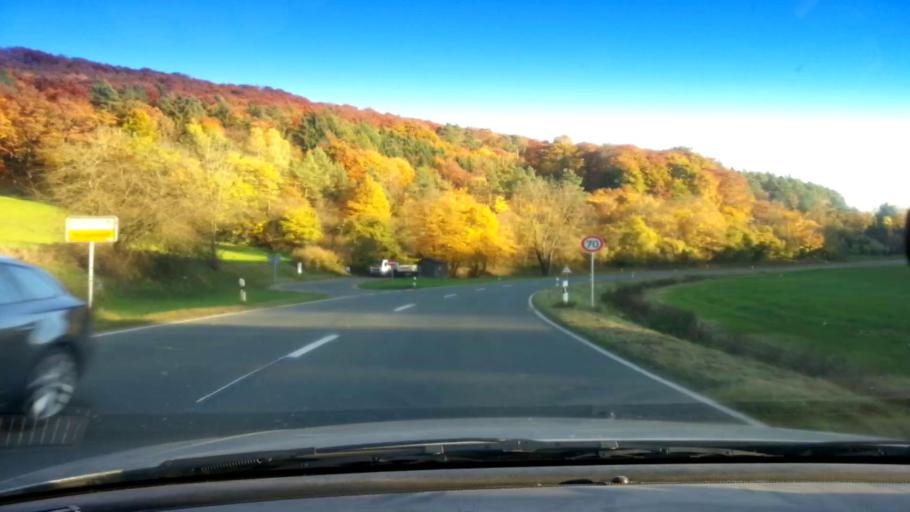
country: DE
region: Bavaria
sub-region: Upper Franconia
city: Heiligenstadt
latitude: 49.8620
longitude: 11.1766
